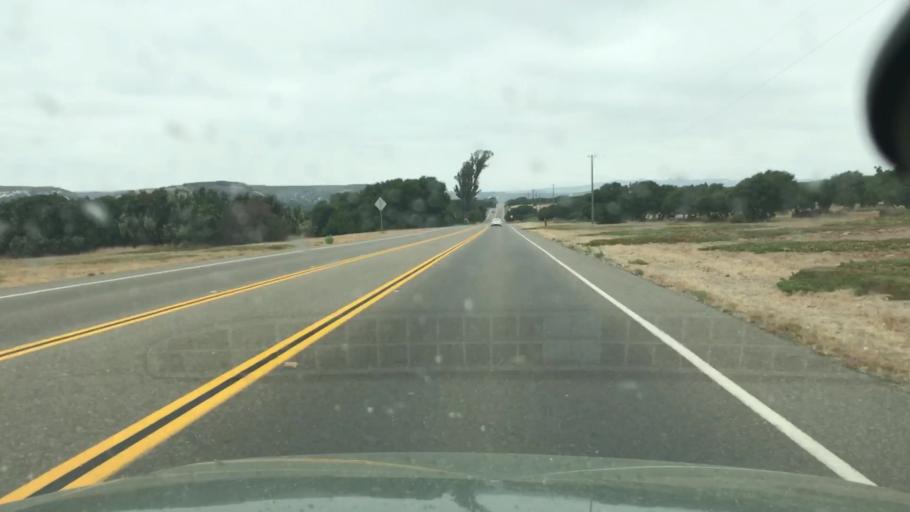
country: US
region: California
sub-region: Santa Barbara County
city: Vandenberg Village
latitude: 34.6863
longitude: -120.5019
